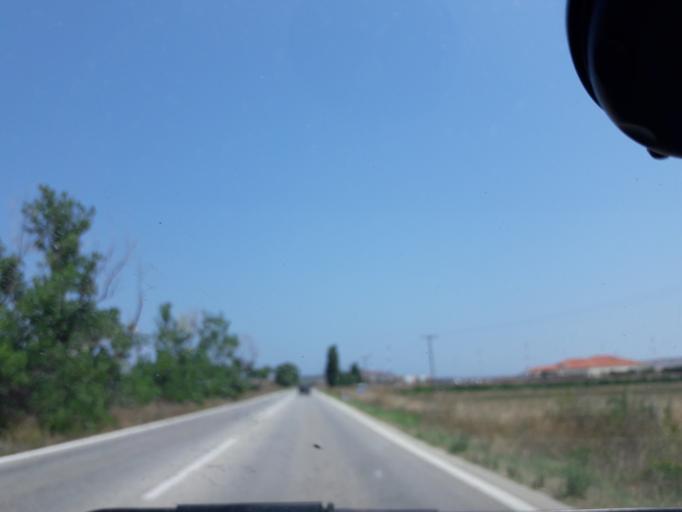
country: GR
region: North Aegean
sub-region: Nomos Lesvou
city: Myrina
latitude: 39.9223
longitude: 25.2289
